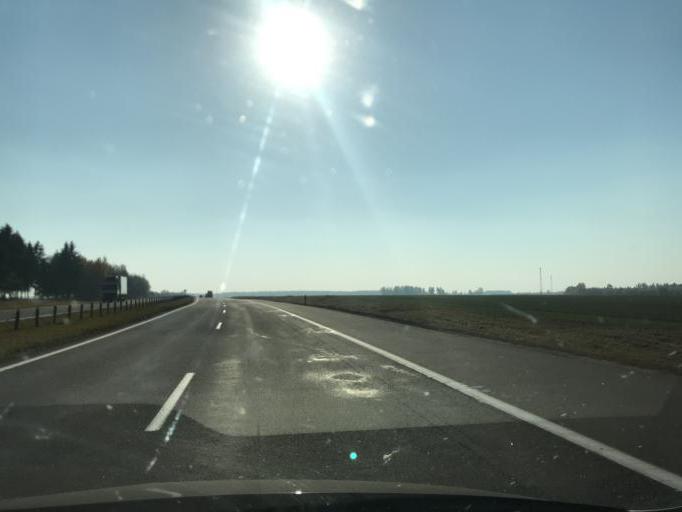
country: BY
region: Minsk
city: Enyerhyetykaw
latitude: 53.6203
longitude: 27.0524
